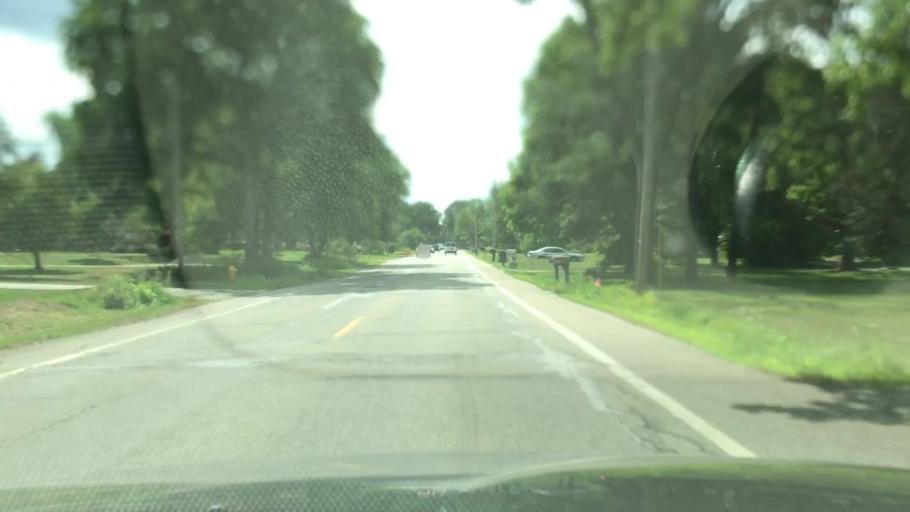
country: US
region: Michigan
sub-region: Kent County
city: East Grand Rapids
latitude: 42.9700
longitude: -85.6070
